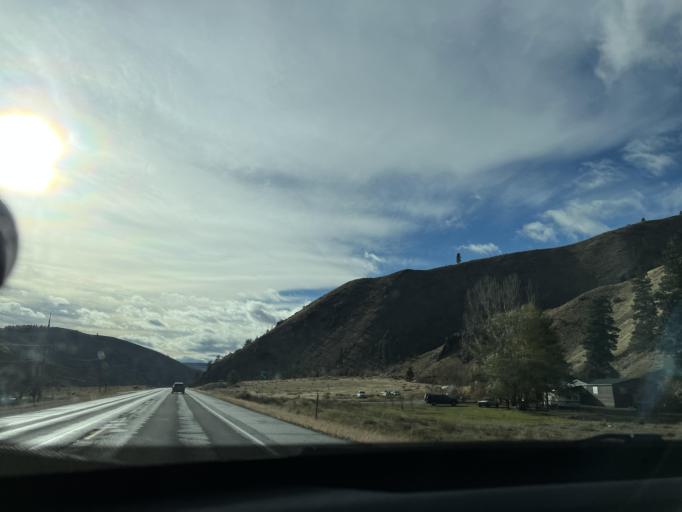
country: US
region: Washington
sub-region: Chelan County
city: Manson
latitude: 47.8087
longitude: -120.1332
